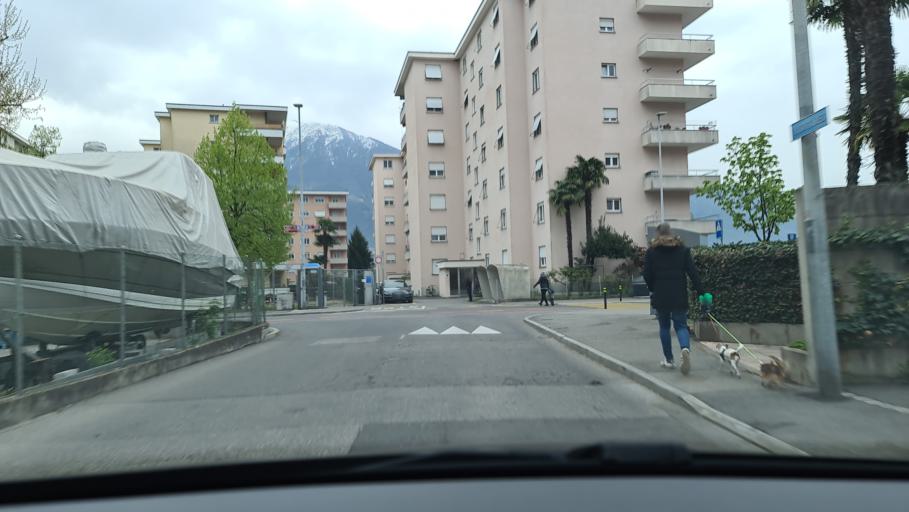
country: CH
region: Ticino
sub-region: Locarno District
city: Locarno
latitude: 46.1615
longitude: 8.7963
